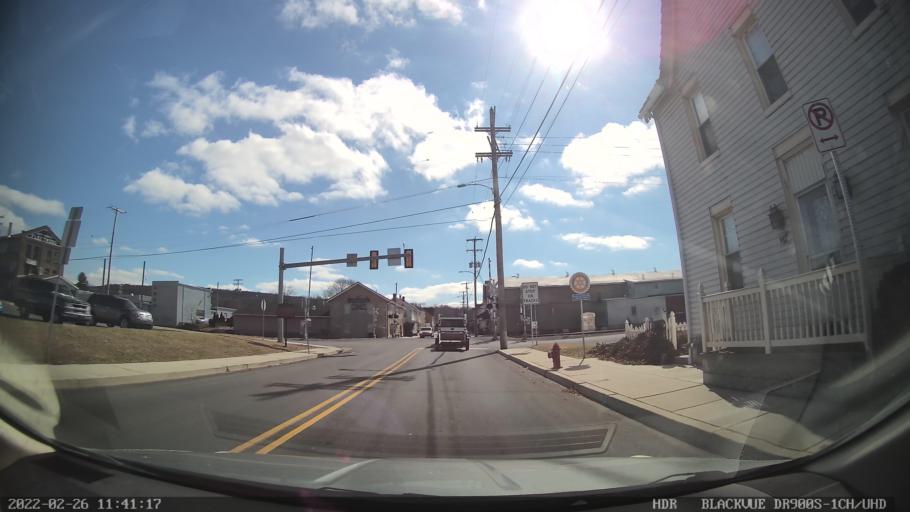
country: US
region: Pennsylvania
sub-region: Berks County
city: Fleetwood
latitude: 40.4524
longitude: -75.8196
